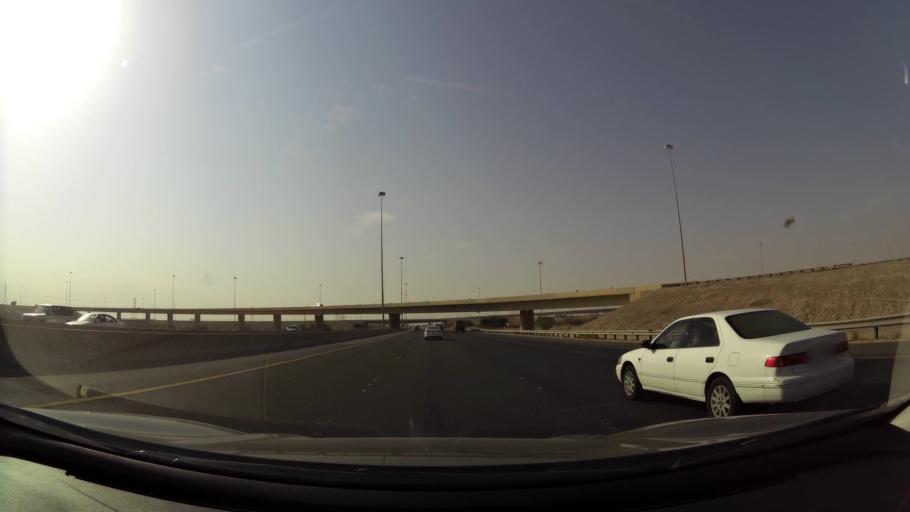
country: KW
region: Al Ahmadi
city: Al Ahmadi
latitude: 29.0368
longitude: 48.0928
